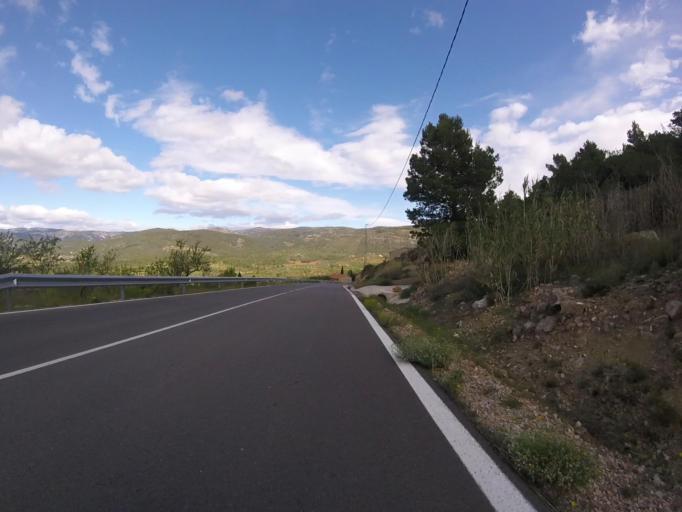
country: ES
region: Valencia
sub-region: Provincia de Castello
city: Culla
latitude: 40.2746
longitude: -0.1106
